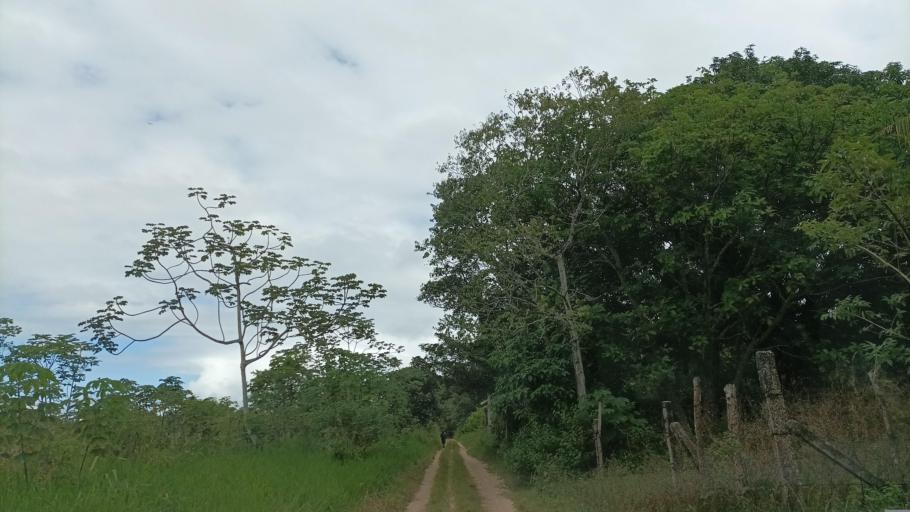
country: MX
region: Veracruz
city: Minatitlan
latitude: 18.0418
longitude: -94.5598
